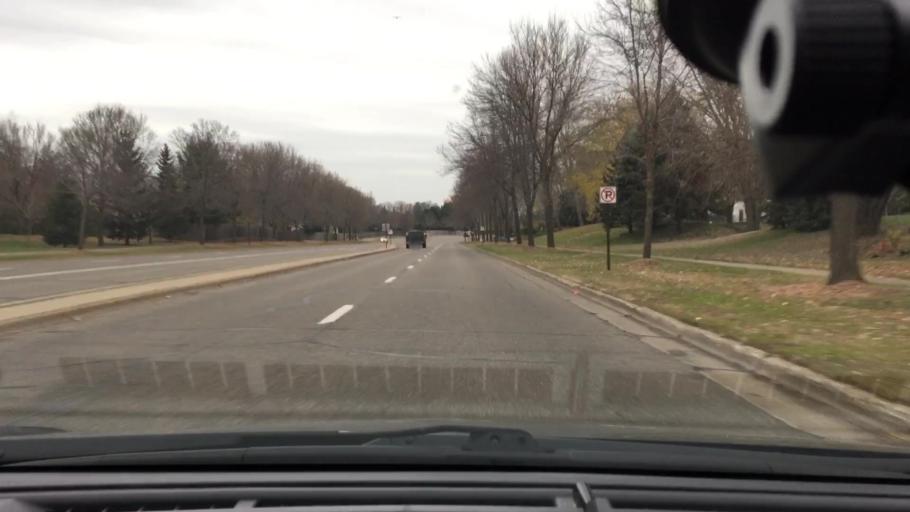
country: US
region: Minnesota
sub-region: Hennepin County
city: Maple Grove
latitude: 45.1133
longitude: -93.4520
